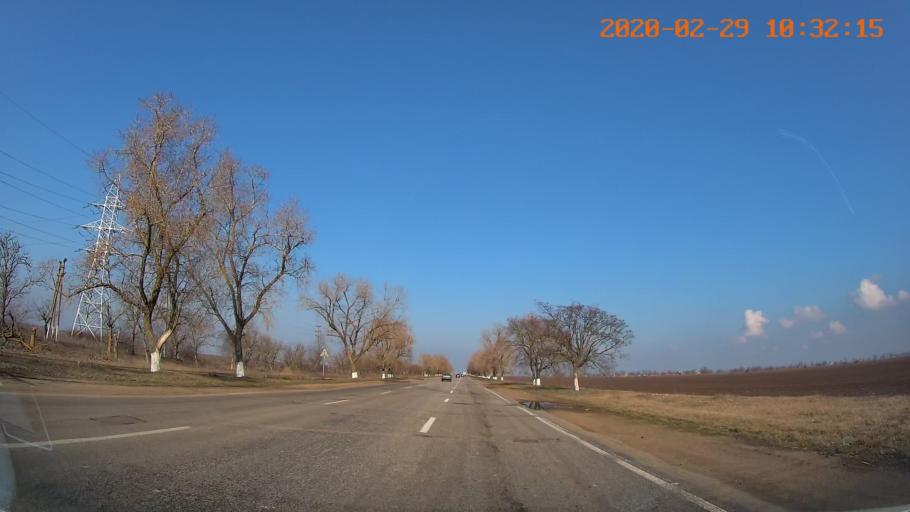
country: UA
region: Odessa
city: Velykoploske
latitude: 46.9587
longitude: 29.5554
